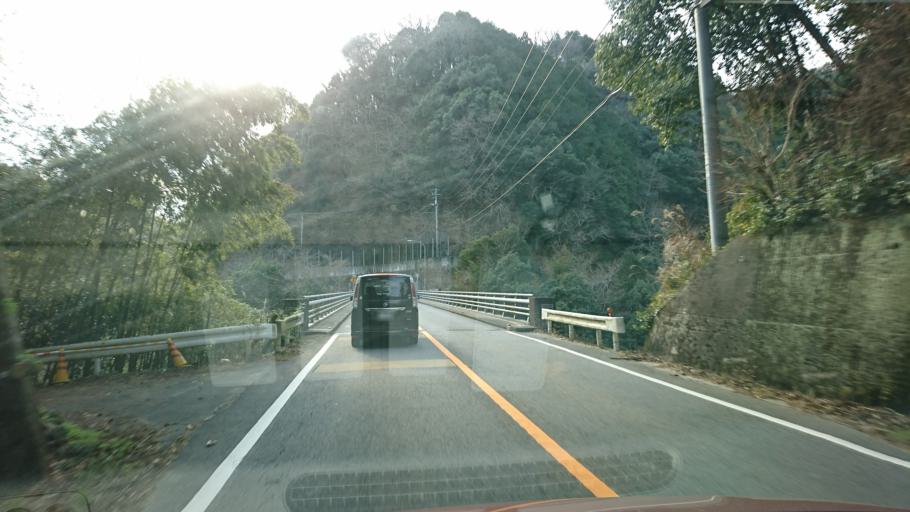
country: JP
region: Ehime
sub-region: Shikoku-chuo Shi
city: Matsuyama
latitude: 33.8942
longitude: 132.8433
